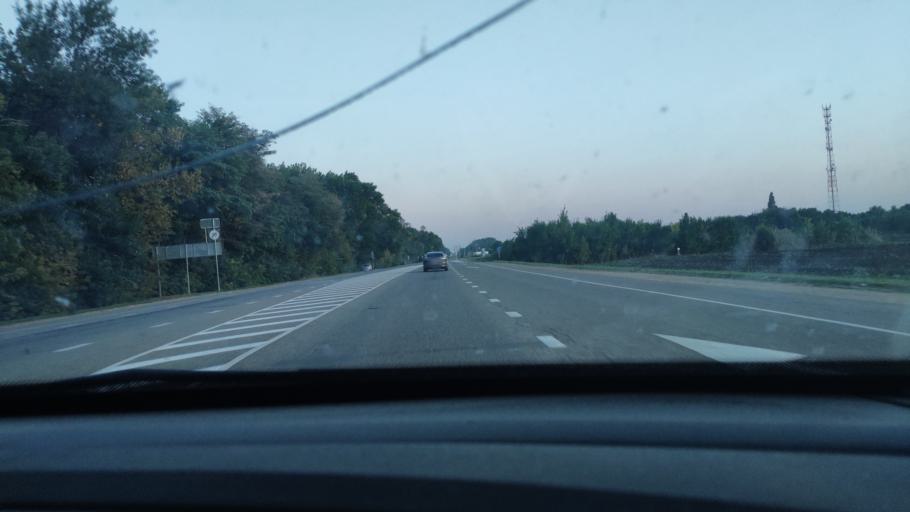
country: RU
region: Krasnodarskiy
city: Medvedovskaya
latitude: 45.4522
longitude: 38.9906
